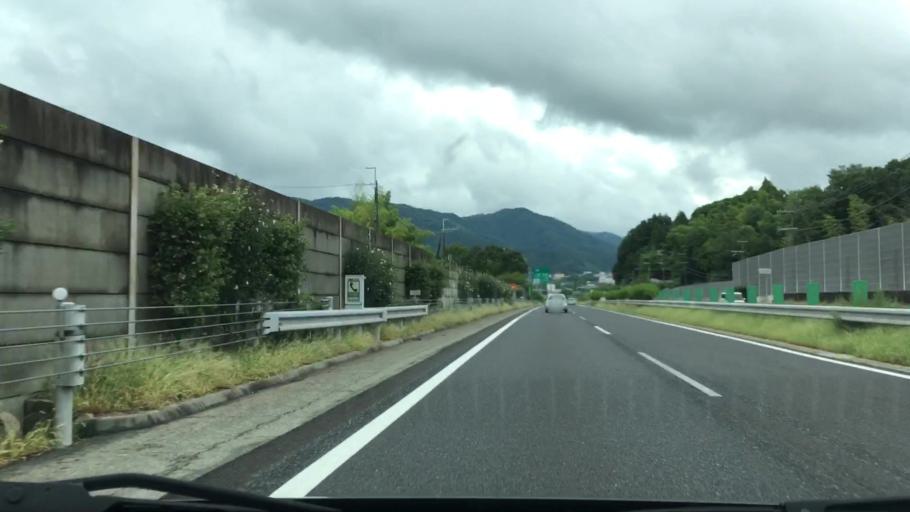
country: JP
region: Hyogo
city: Yamazakicho-nakabirose
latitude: 34.9957
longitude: 134.5636
